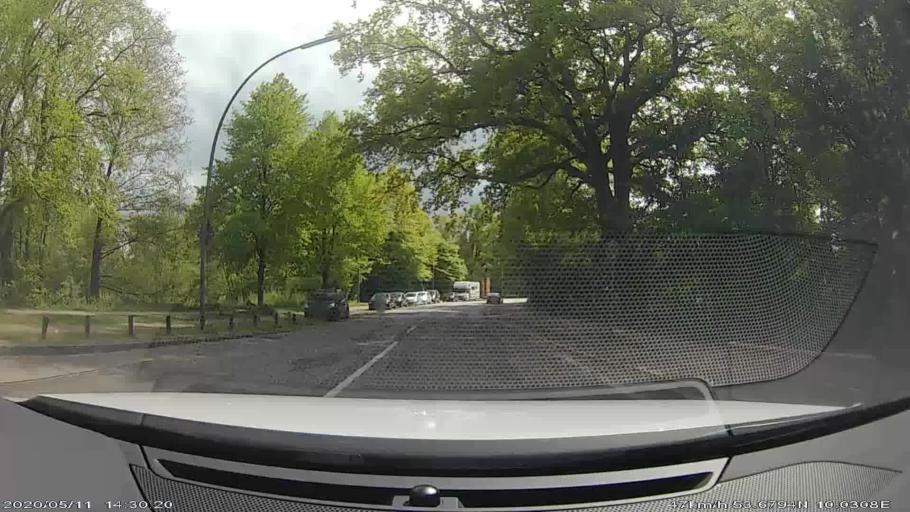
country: DE
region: Hamburg
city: Langenhorn
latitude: 53.6698
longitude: 10.0260
